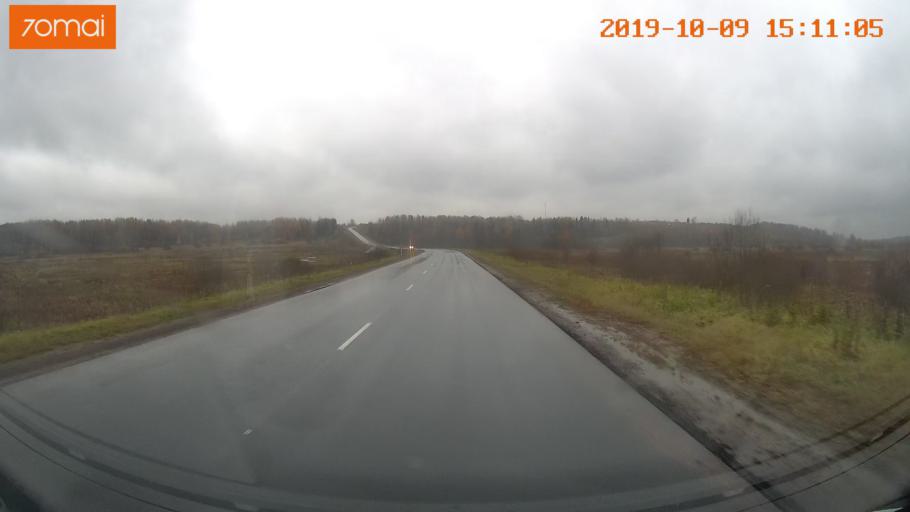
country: RU
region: Kostroma
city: Susanino
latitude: 58.1699
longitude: 41.6325
